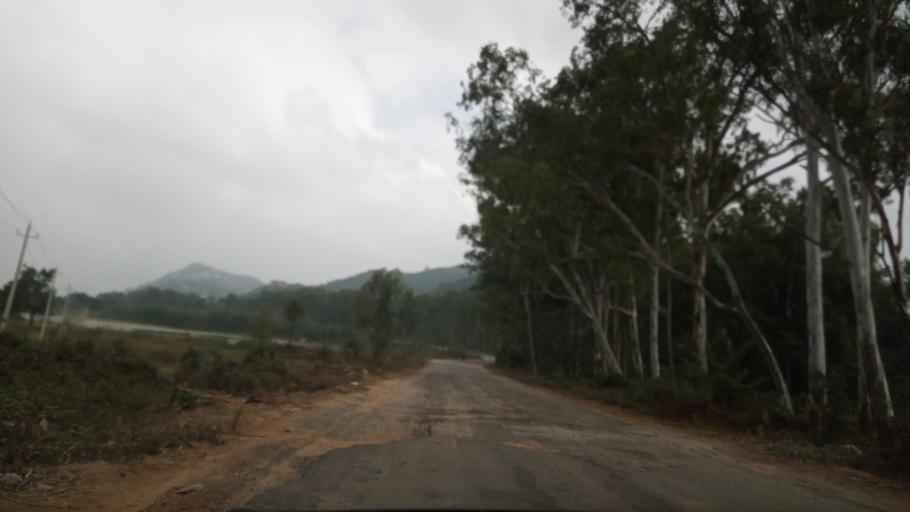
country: IN
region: Andhra Pradesh
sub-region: Chittoor
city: Madanapalle
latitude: 13.5035
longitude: 78.3322
